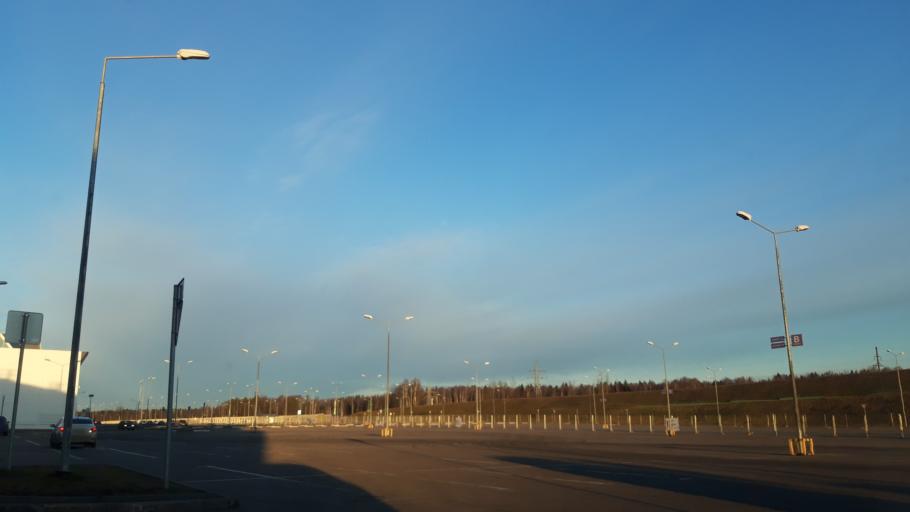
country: RU
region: Moskovskaya
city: Rzhavki
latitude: 55.9989
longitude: 37.2621
